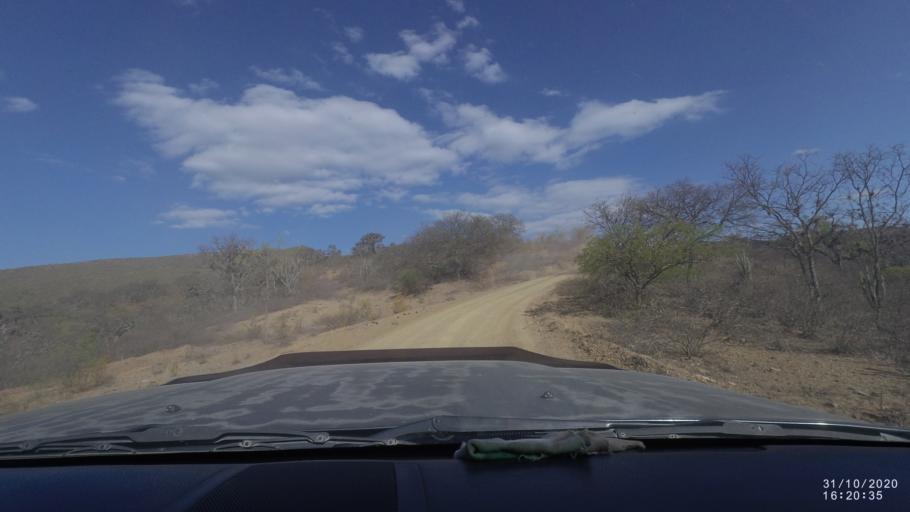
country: BO
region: Chuquisaca
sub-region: Provincia Zudanez
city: Mojocoya
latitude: -18.3975
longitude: -64.6010
